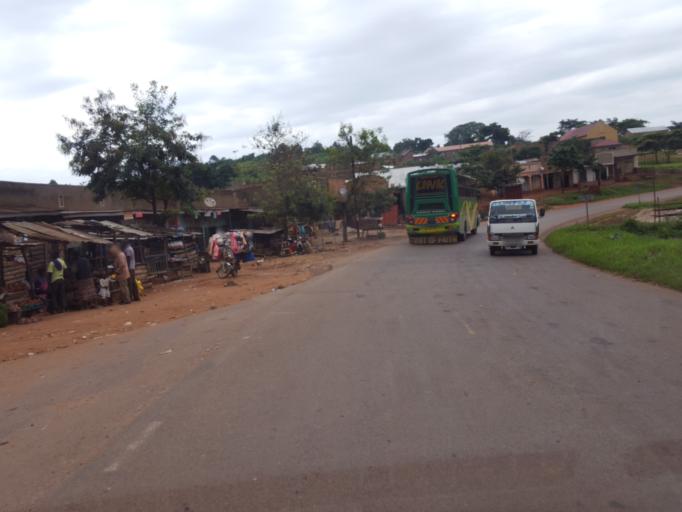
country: UG
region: Central Region
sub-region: Mityana District
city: Mityana
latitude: 0.6725
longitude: 32.0862
